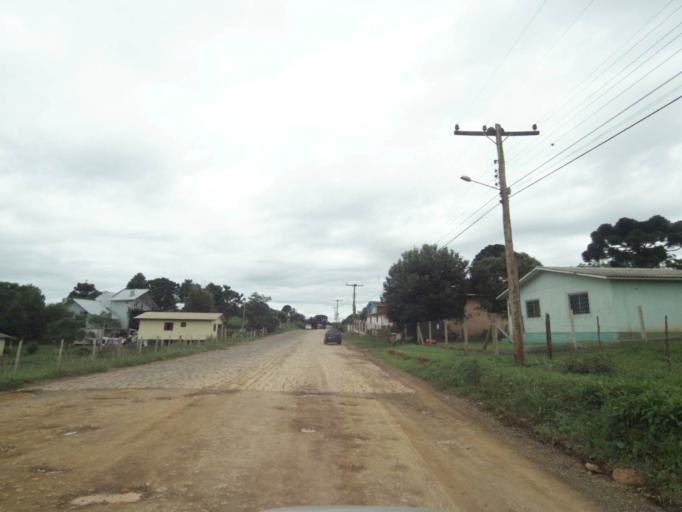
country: BR
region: Rio Grande do Sul
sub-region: Lagoa Vermelha
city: Lagoa Vermelha
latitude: -28.2202
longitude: -51.5373
